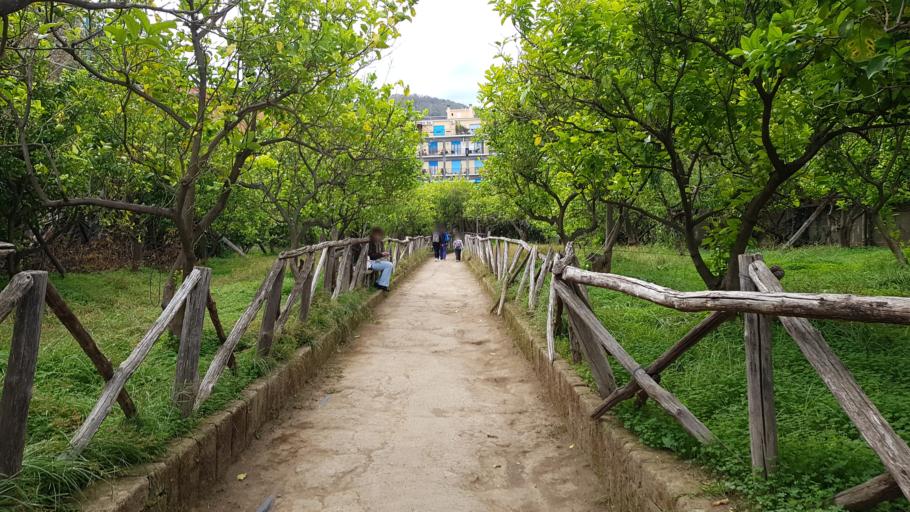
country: IT
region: Campania
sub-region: Provincia di Napoli
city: Sorrento
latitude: 40.6278
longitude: 14.3807
